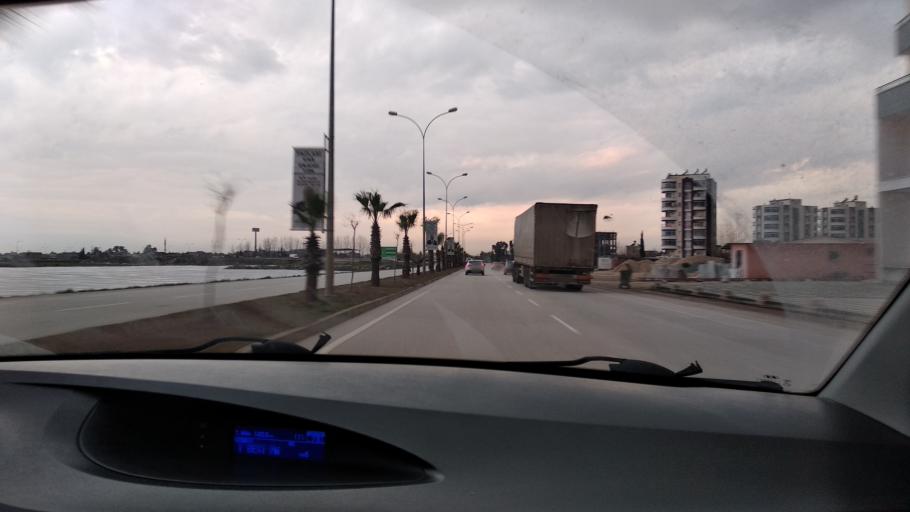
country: TR
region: Adana
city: Yuregir
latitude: 37.0107
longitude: 35.3942
